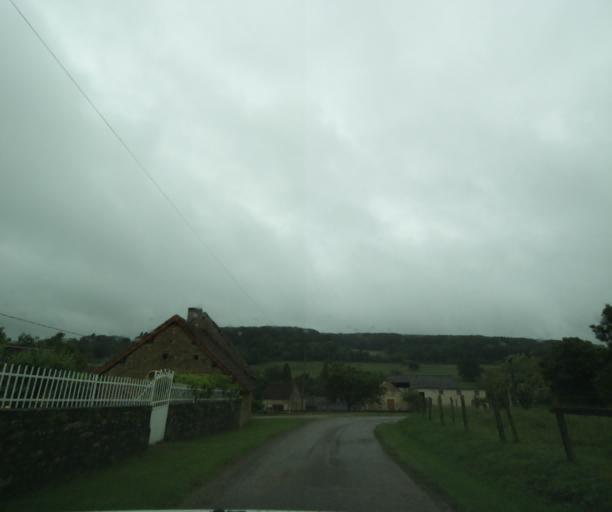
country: FR
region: Bourgogne
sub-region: Departement de Saone-et-Loire
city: Charolles
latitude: 46.4054
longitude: 4.3265
